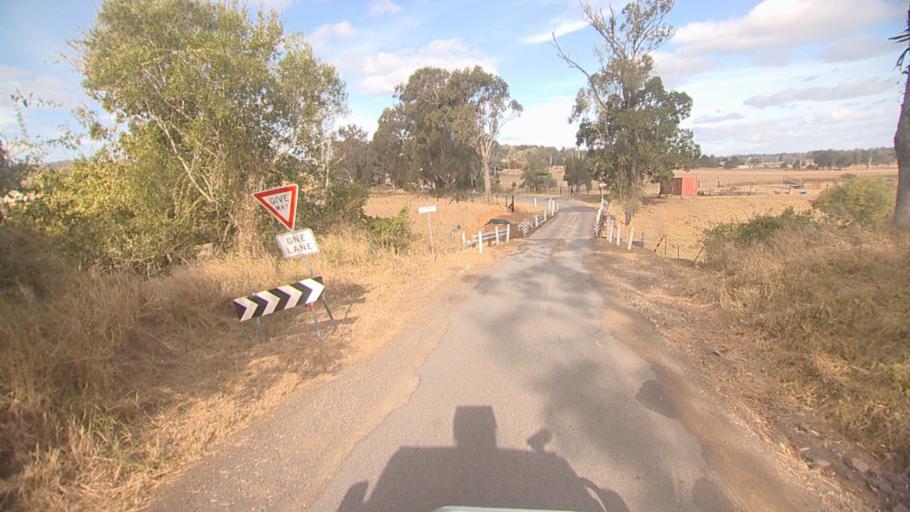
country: AU
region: Queensland
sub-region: Logan
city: Cedar Vale
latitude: -27.9170
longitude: 153.0002
